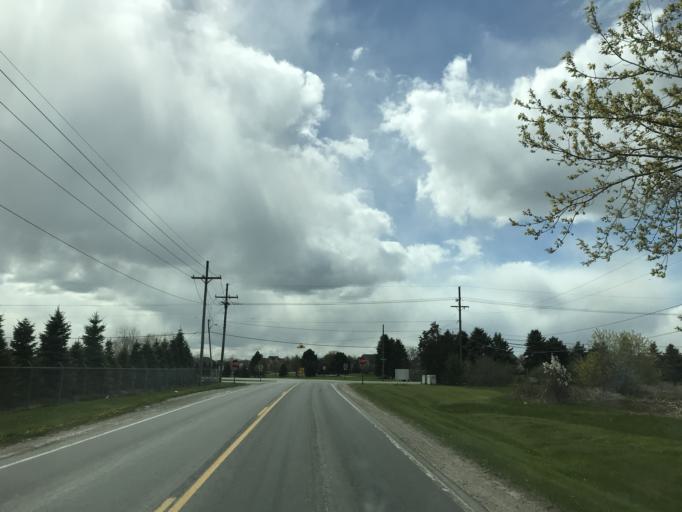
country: US
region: Michigan
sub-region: Wayne County
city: Plymouth
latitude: 42.3740
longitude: -83.5673
